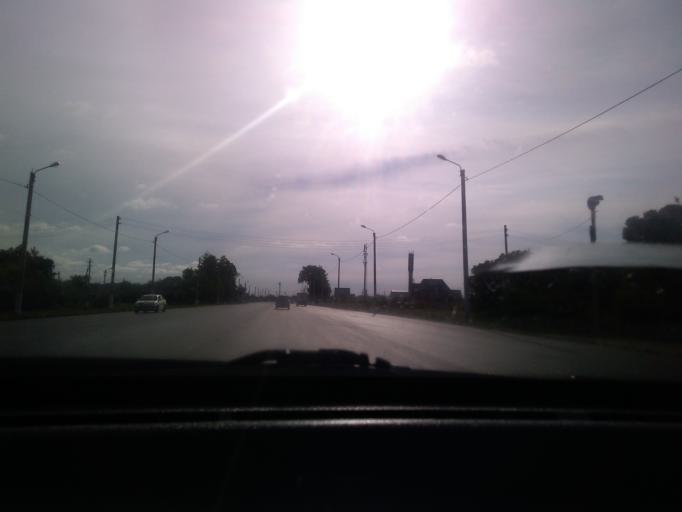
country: RU
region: Kursk
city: Voroshnevo
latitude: 51.6539
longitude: 36.0018
